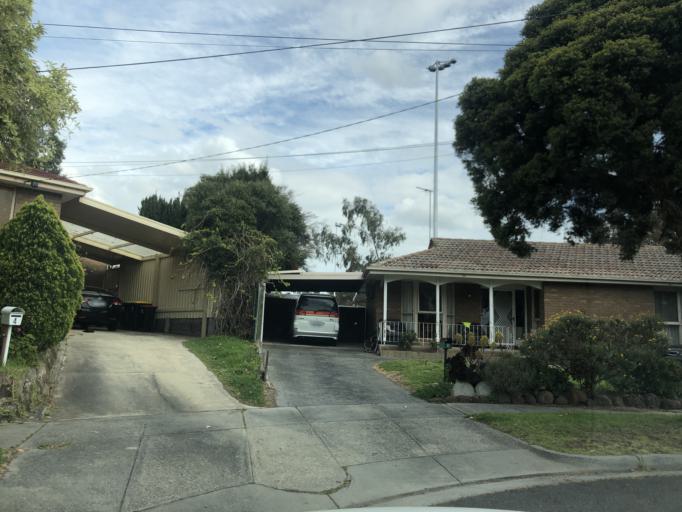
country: AU
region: Victoria
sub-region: Greater Dandenong
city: Noble Park North
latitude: -37.9523
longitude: 145.1952
